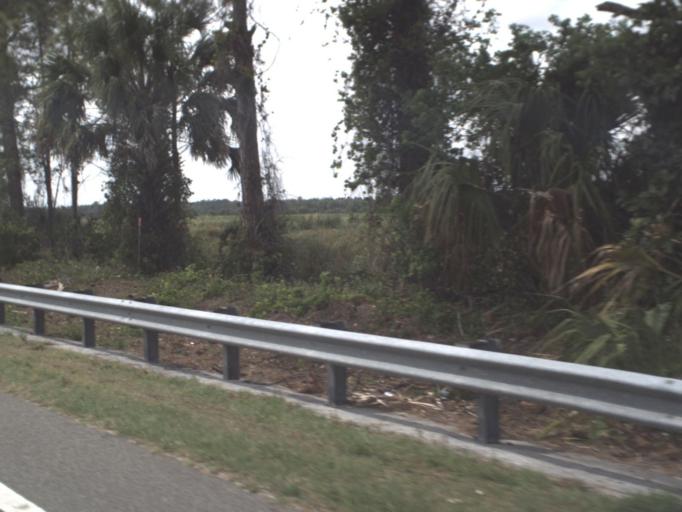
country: US
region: Florida
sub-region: Flagler County
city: Bunnell
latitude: 29.4821
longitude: -81.3603
